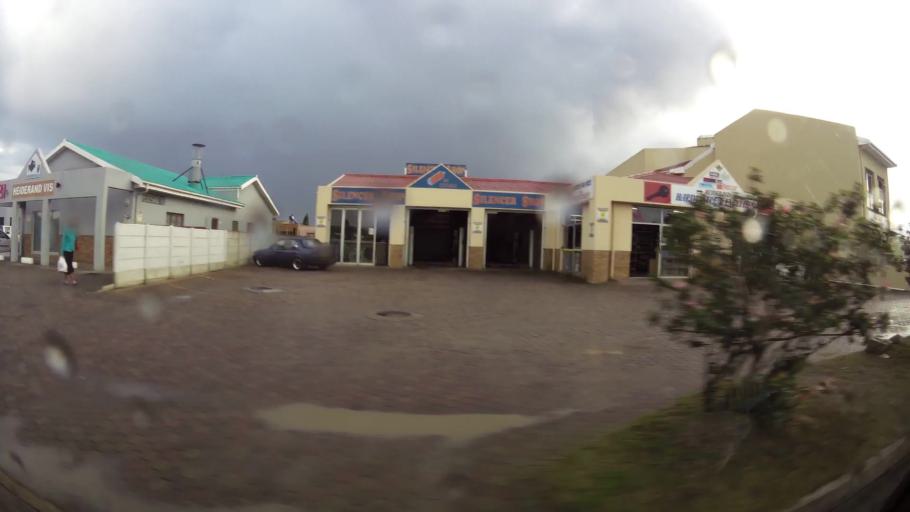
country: ZA
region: Western Cape
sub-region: Eden District Municipality
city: Mossel Bay
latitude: -34.1842
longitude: 22.1141
